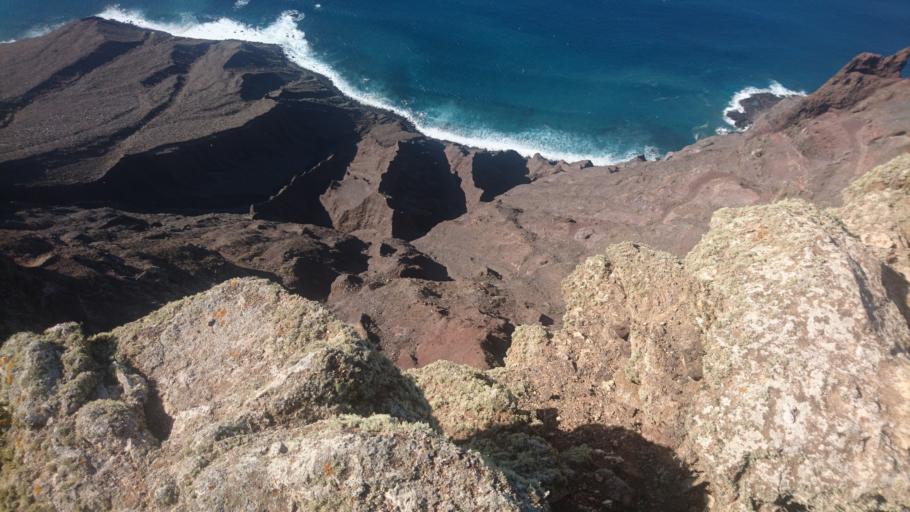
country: ES
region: Canary Islands
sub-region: Provincia de Las Palmas
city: Haria
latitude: 29.1702
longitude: -13.5125
